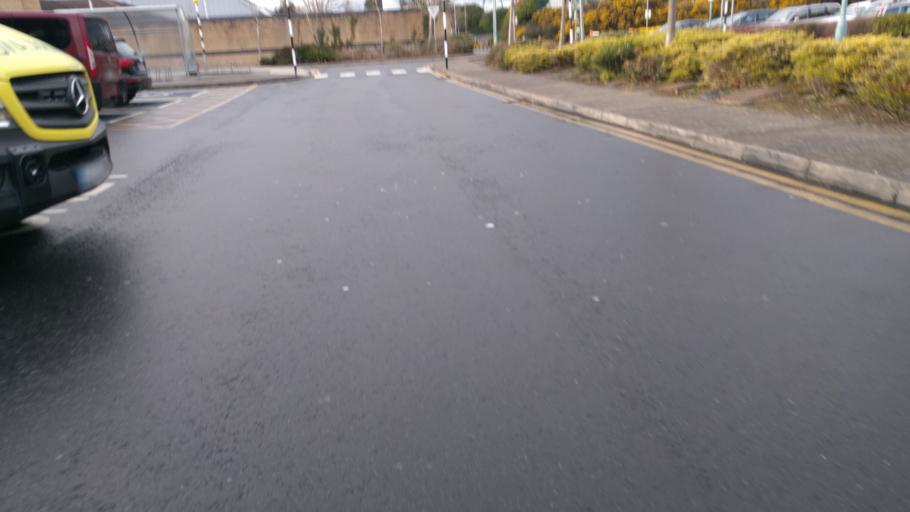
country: IE
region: Leinster
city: Tallaght
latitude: 53.2919
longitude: -6.3781
